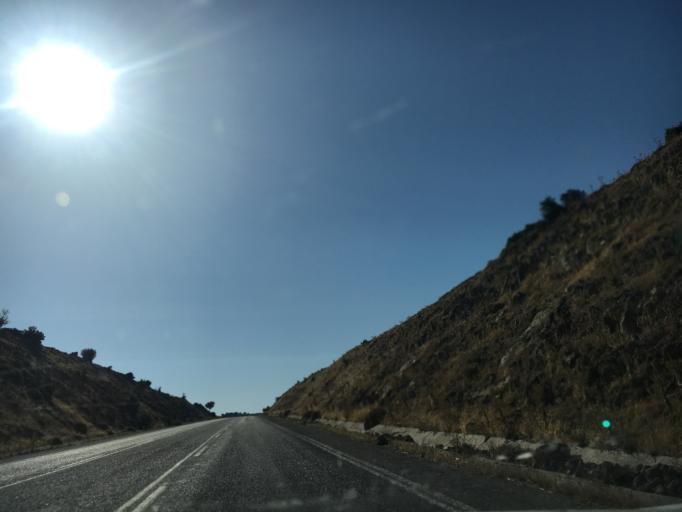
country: TR
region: Canakkale
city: Behram
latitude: 39.5072
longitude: 26.3909
